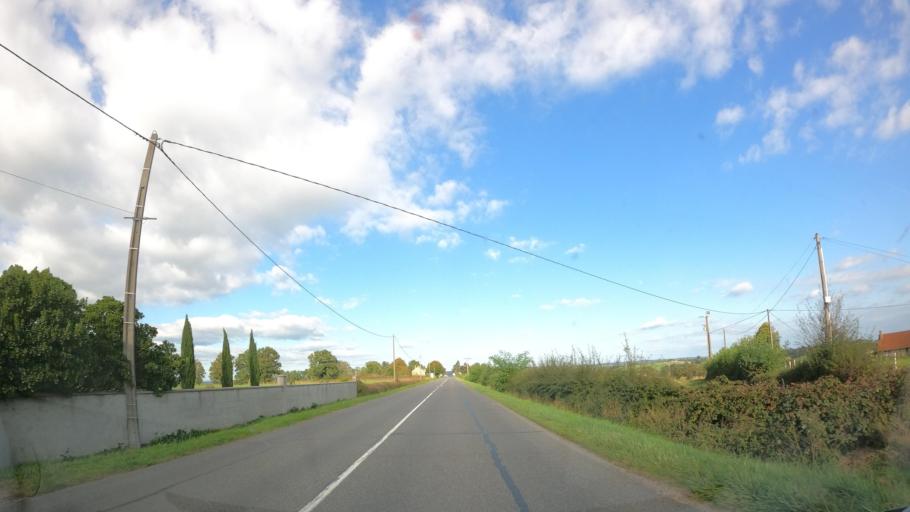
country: FR
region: Auvergne
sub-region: Departement de l'Allier
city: Dompierre-sur-Besbre
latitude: 46.5229
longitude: 3.7119
